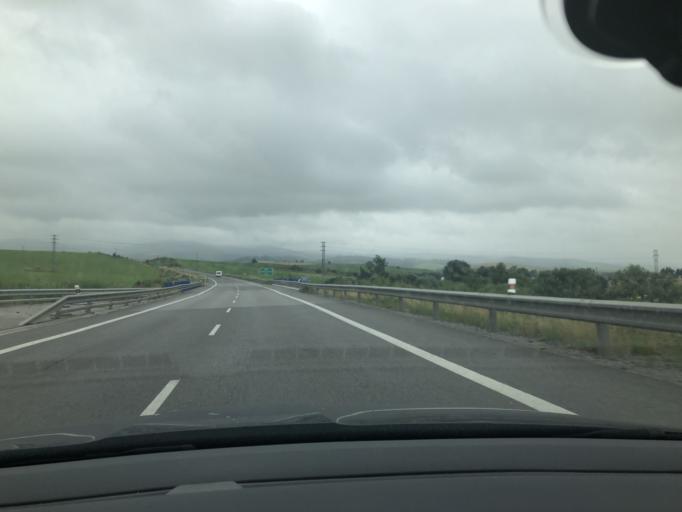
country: SK
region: Zilinsky
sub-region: Okres Zilina
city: Trstena
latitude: 49.3735
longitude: 19.6298
